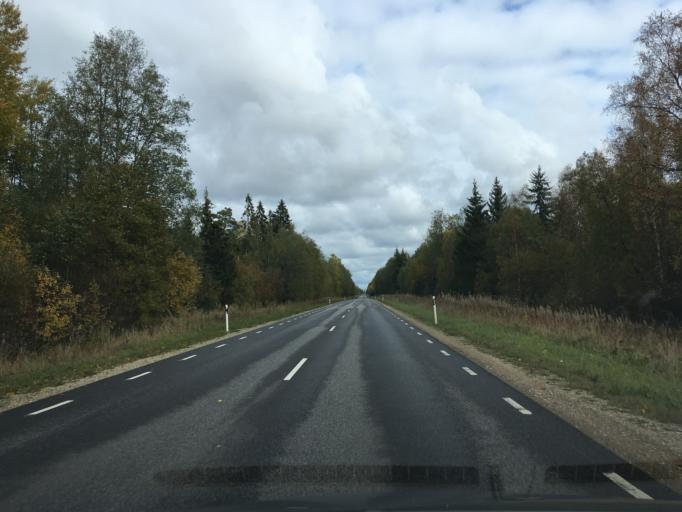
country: EE
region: Harju
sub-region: Anija vald
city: Kehra
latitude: 59.2284
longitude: 25.2770
